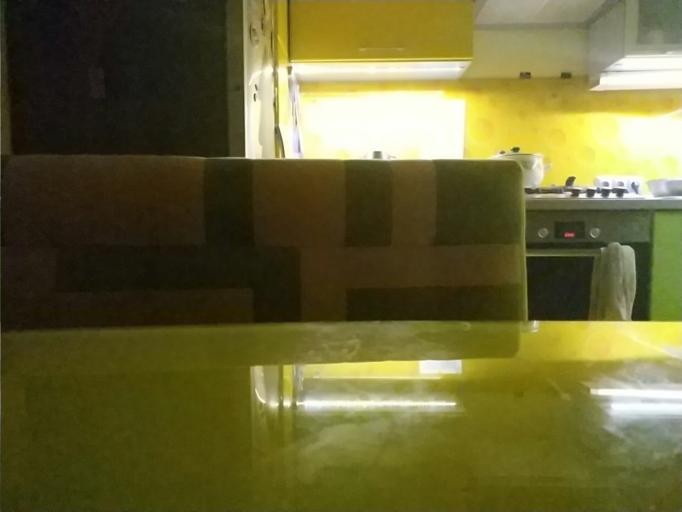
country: RU
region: Republic of Karelia
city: Pyaozerskiy
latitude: 65.7947
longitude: 30.4754
